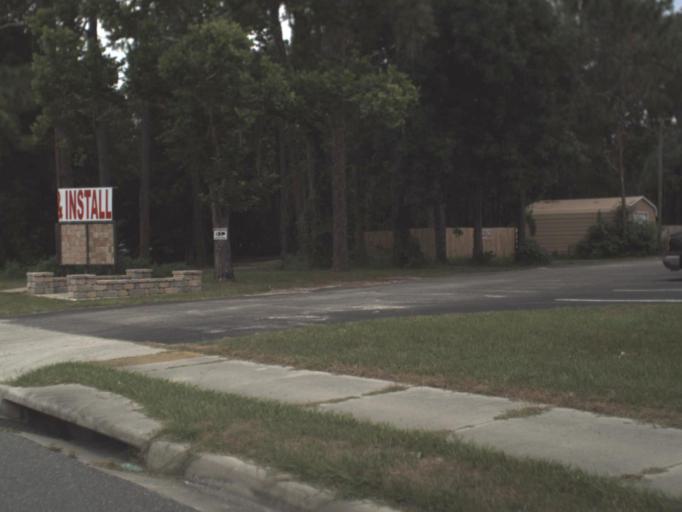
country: US
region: Florida
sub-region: Citrus County
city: Crystal River
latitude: 28.8958
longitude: -82.5587
